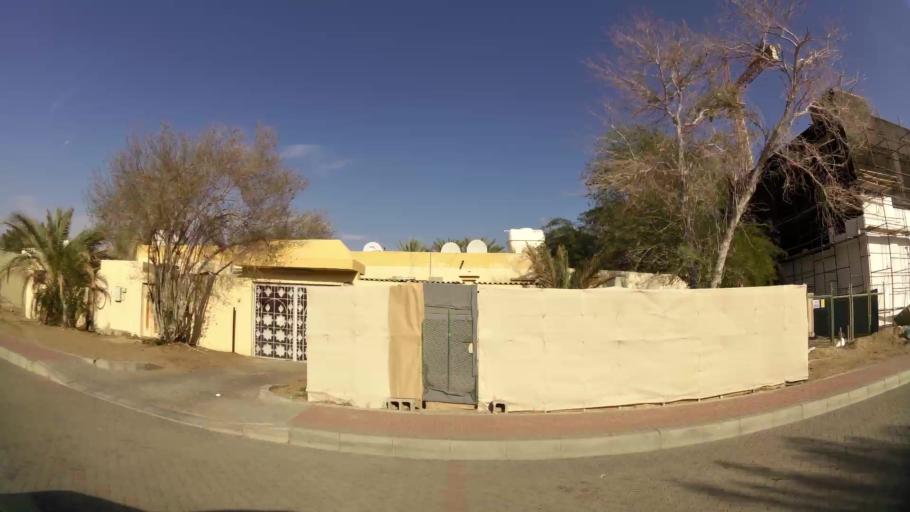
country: AE
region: Abu Dhabi
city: Al Ain
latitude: 24.0364
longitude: 55.8431
